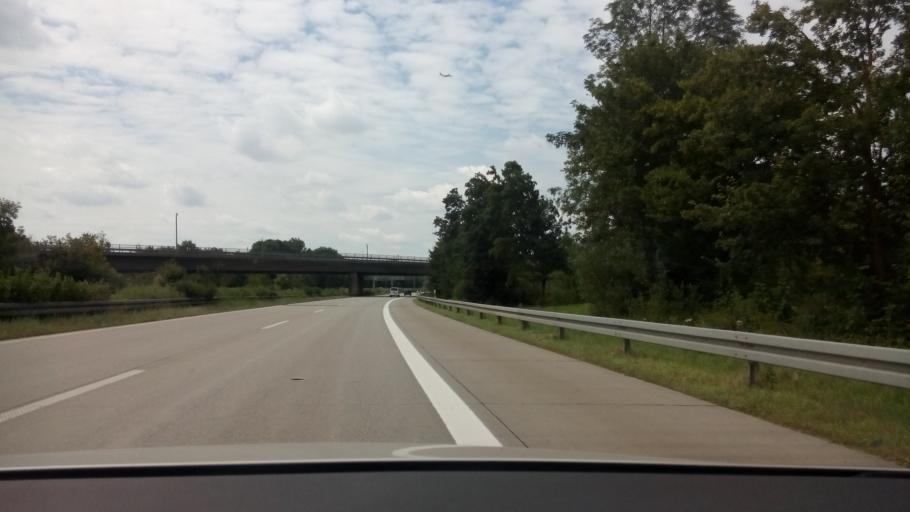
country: DE
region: Bavaria
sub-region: Upper Bavaria
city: Hallbergmoos
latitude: 48.3525
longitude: 11.7290
